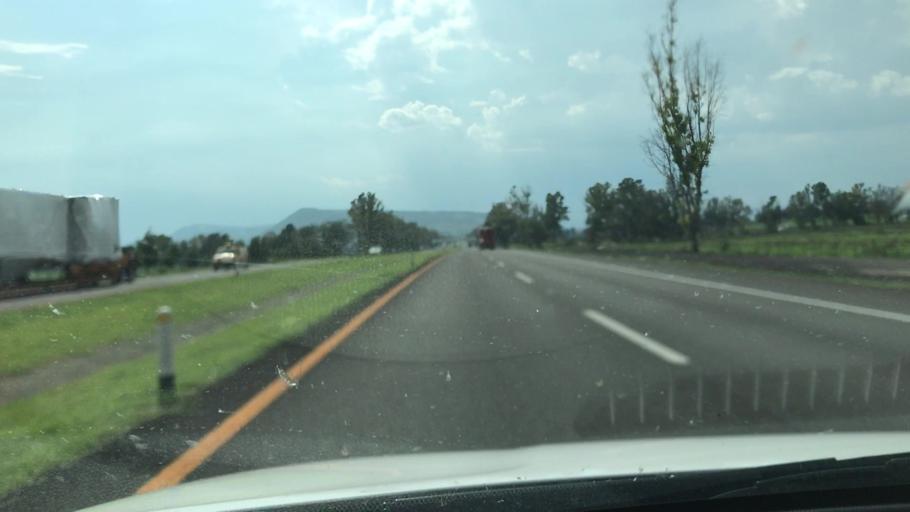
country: MX
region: Jalisco
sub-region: Ocotlan
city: Joconoxtle (La Tuna)
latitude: 20.3833
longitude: -102.7044
